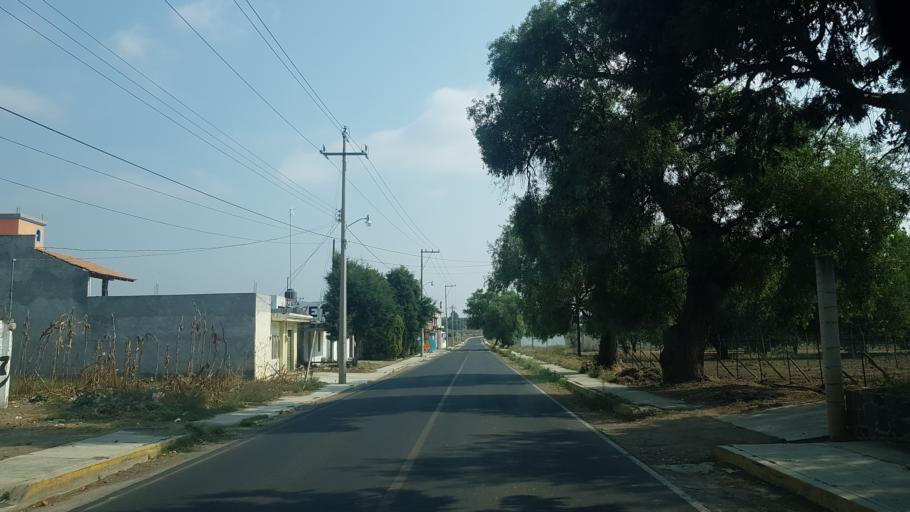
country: MX
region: Puebla
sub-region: Huejotzingo
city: San Juan Pancoac
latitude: 19.1192
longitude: -98.4249
